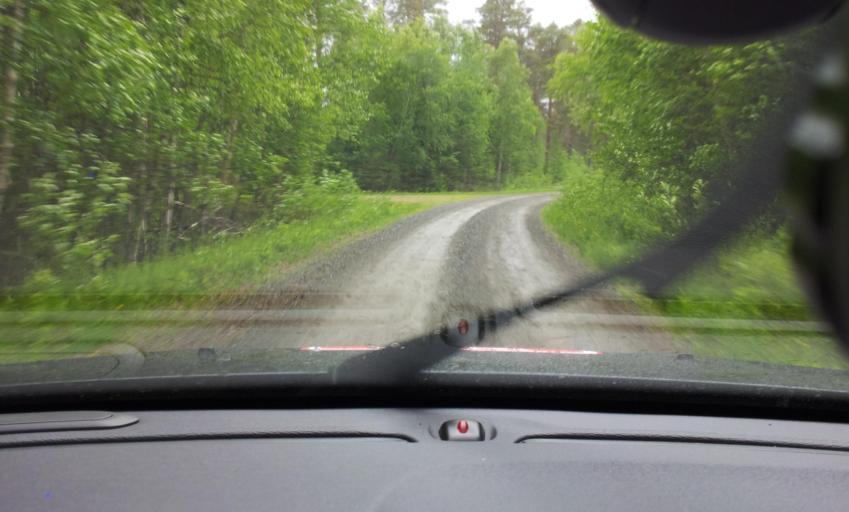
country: SE
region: Jaemtland
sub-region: Are Kommun
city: Are
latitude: 63.1812
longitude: 13.1237
